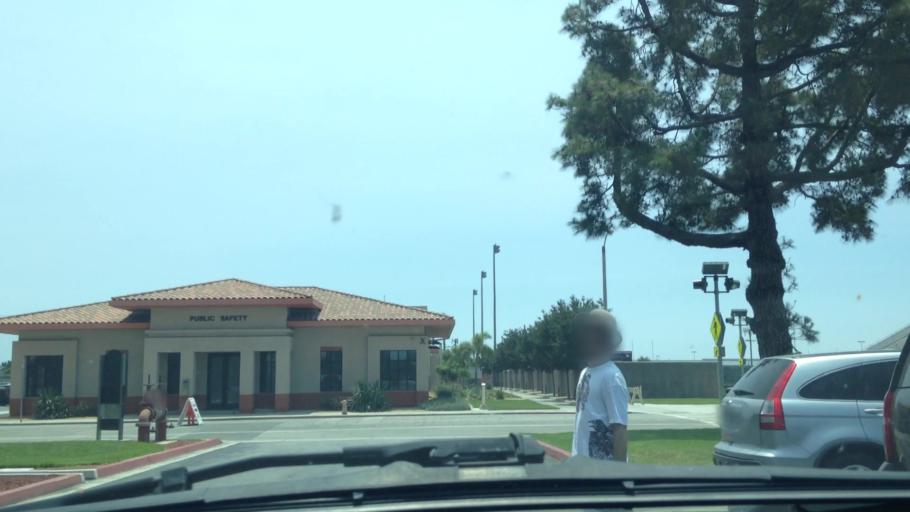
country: US
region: California
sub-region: Los Angeles County
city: Lakewood
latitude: 33.8303
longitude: -118.1356
